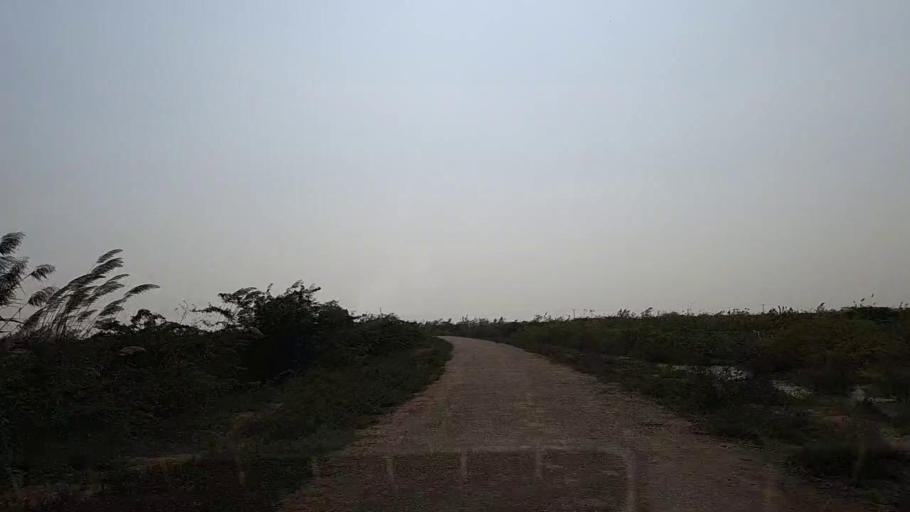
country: PK
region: Sindh
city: Mirpur Sakro
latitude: 24.6527
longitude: 67.6906
